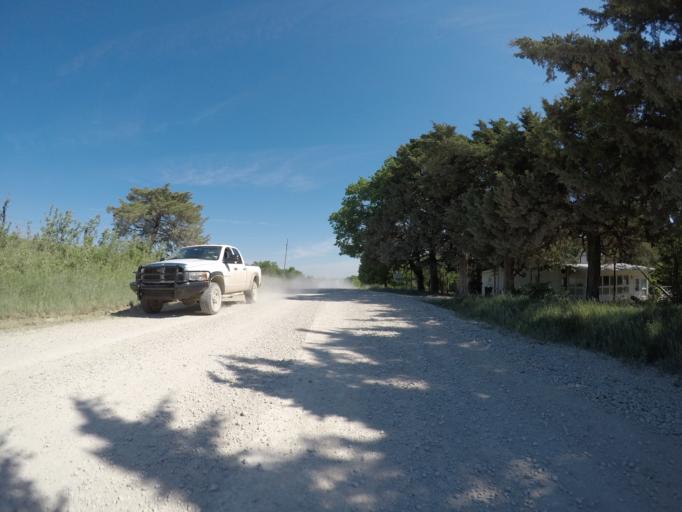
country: US
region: Kansas
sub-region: Wabaunsee County
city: Alma
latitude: 38.9893
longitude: -96.1138
